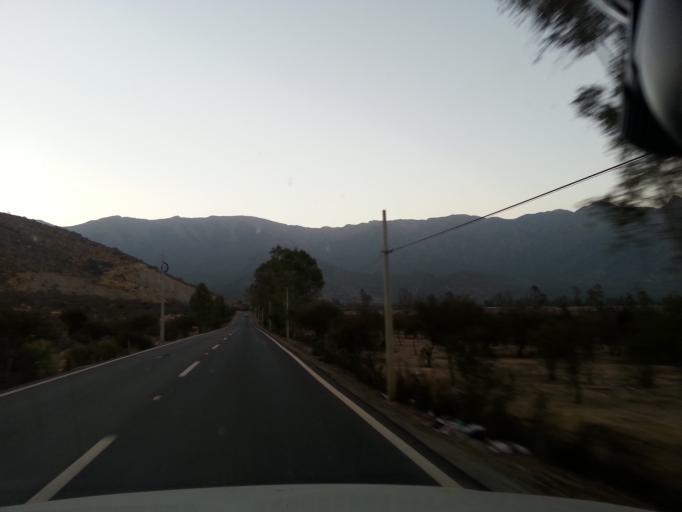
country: CL
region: Santiago Metropolitan
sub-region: Provincia de Chacabuco
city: Lampa
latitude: -33.2457
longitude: -70.9165
